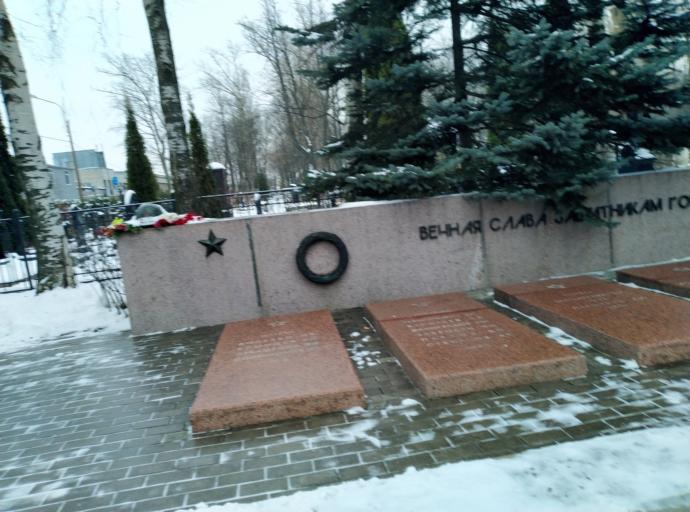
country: RU
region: St.-Petersburg
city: Centralniy
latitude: 59.9028
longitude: 30.3563
